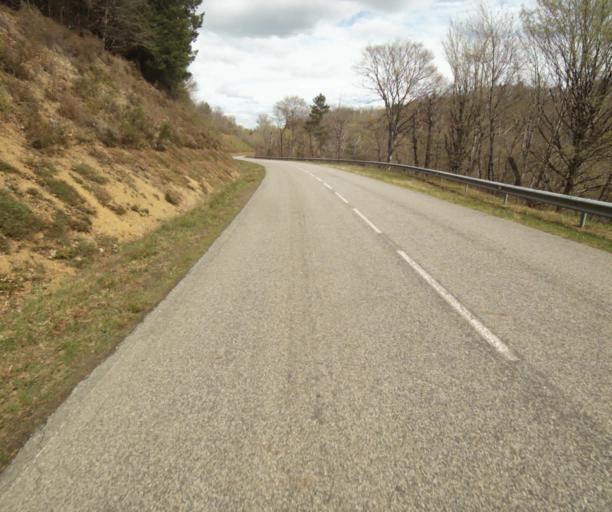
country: FR
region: Limousin
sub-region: Departement de la Correze
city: Laguenne
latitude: 45.2059
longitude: 1.8631
